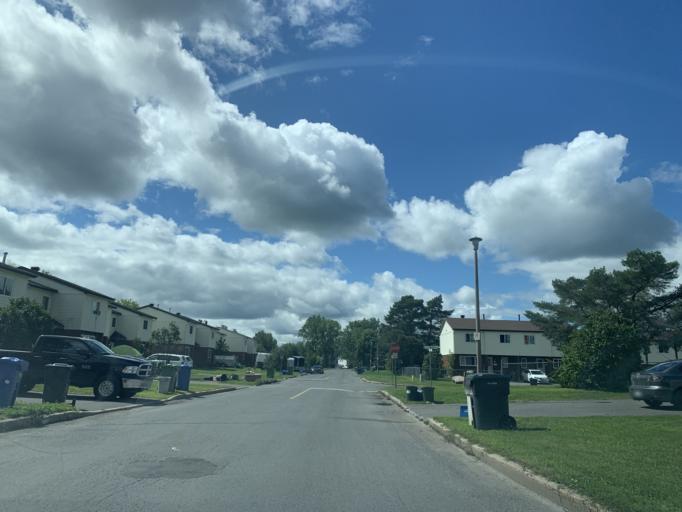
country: CA
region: Ontario
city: Hawkesbury
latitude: 45.6028
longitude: -74.6128
